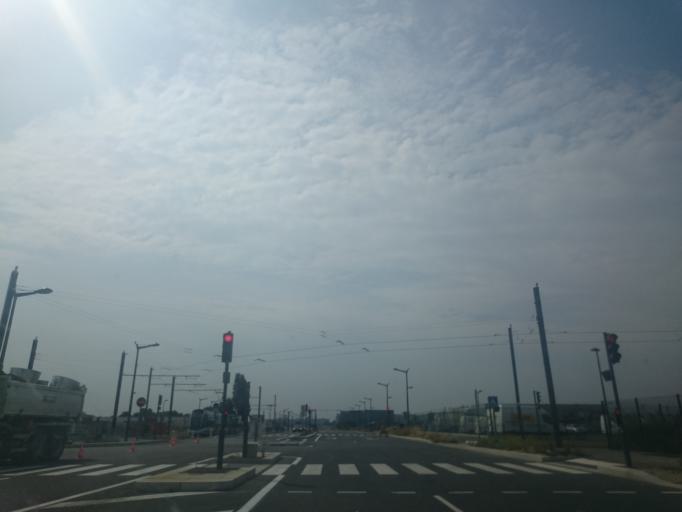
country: FR
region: Ile-de-France
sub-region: Departement du Val-de-Marne
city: Rungis
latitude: 48.7399
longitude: 2.3696
